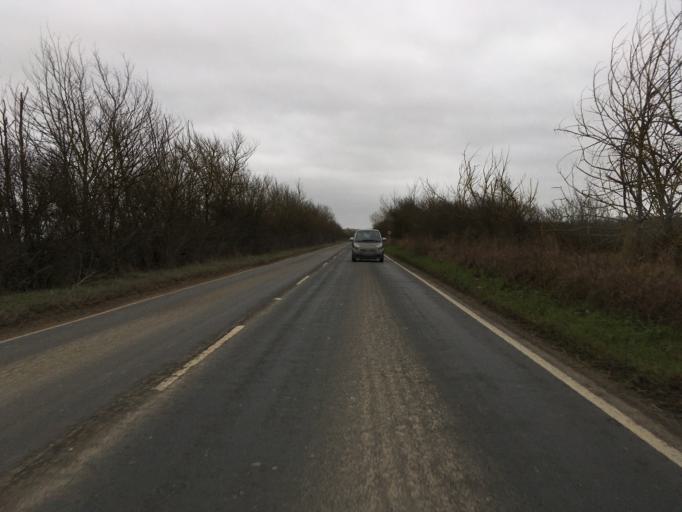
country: GB
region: England
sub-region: Oxfordshire
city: Stanford in the Vale
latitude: 51.6273
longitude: -1.5023
